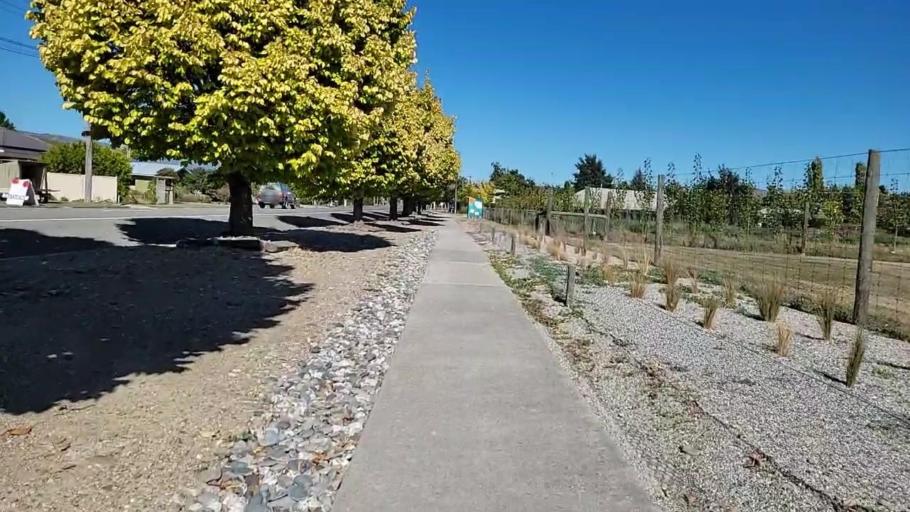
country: NZ
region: Otago
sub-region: Queenstown-Lakes District
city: Wanaka
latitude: -45.0987
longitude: 169.5975
